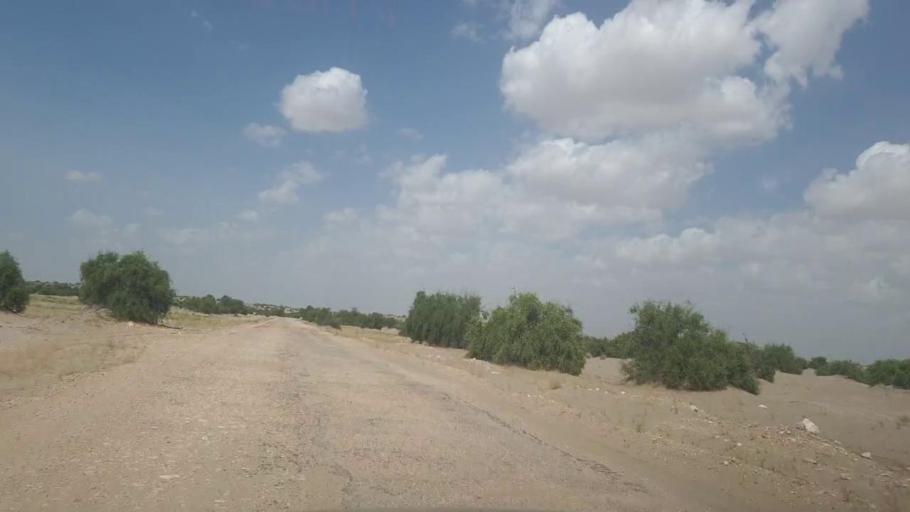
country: PK
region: Sindh
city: Kot Diji
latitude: 27.2647
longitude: 69.1765
